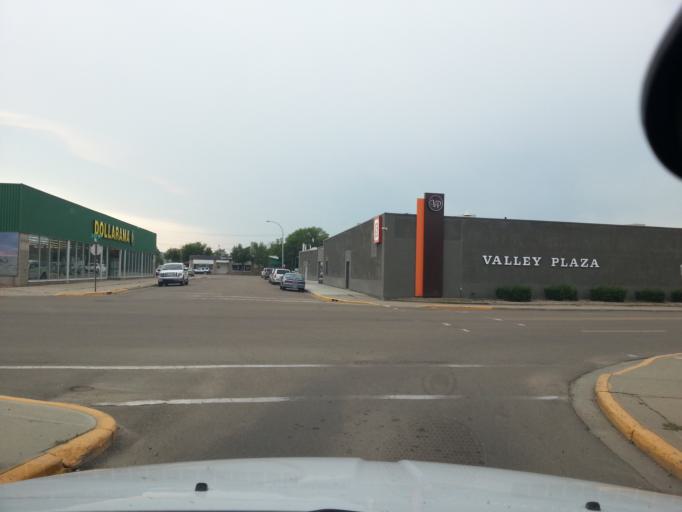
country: CA
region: Alberta
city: Three Hills
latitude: 51.4629
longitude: -112.7104
